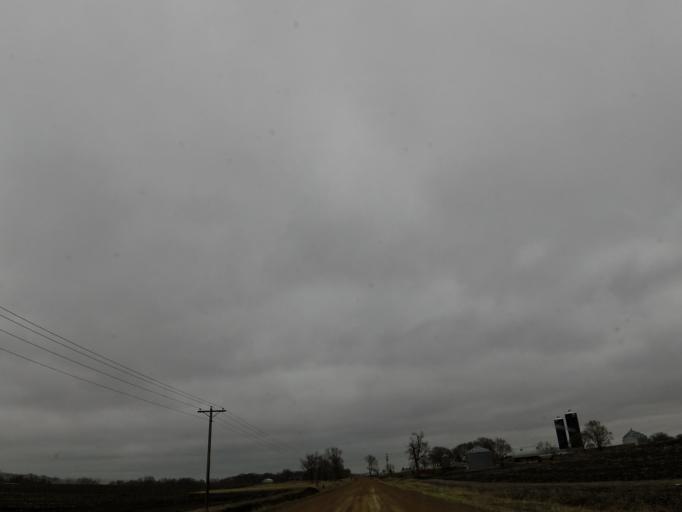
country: US
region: Minnesota
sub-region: Scott County
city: Shakopee
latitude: 44.7032
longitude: -93.5343
